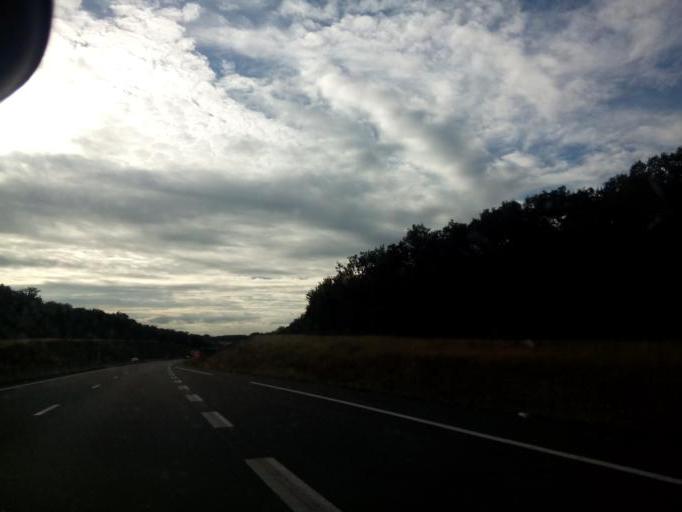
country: FR
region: Centre
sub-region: Departement d'Indre-et-Loire
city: Montbazon
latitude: 47.3025
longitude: 0.6848
